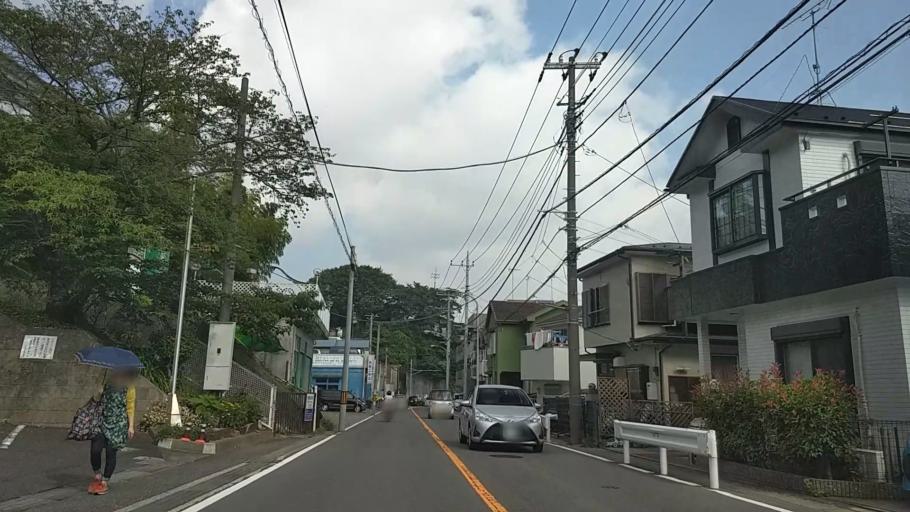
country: JP
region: Kanagawa
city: Yokohama
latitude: 35.4172
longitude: 139.5639
